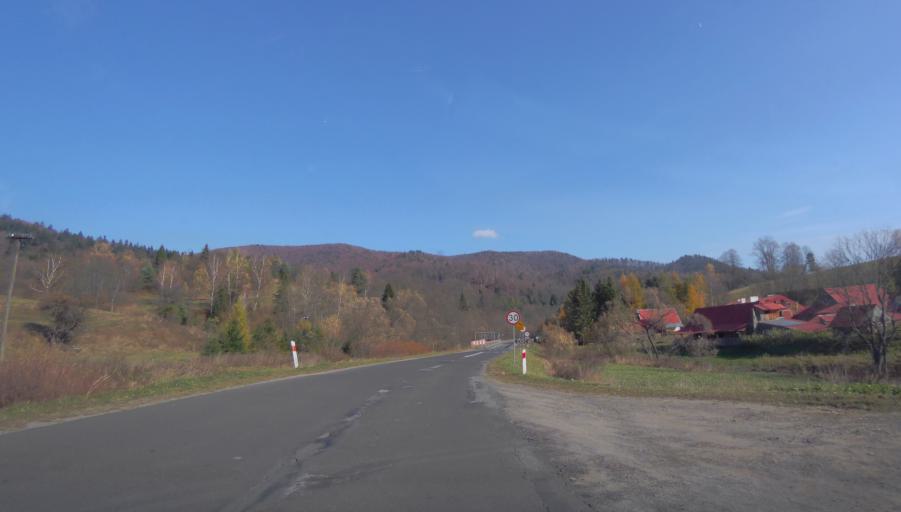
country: PL
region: Subcarpathian Voivodeship
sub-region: Powiat leski
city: Cisna
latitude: 49.2079
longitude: 22.2639
